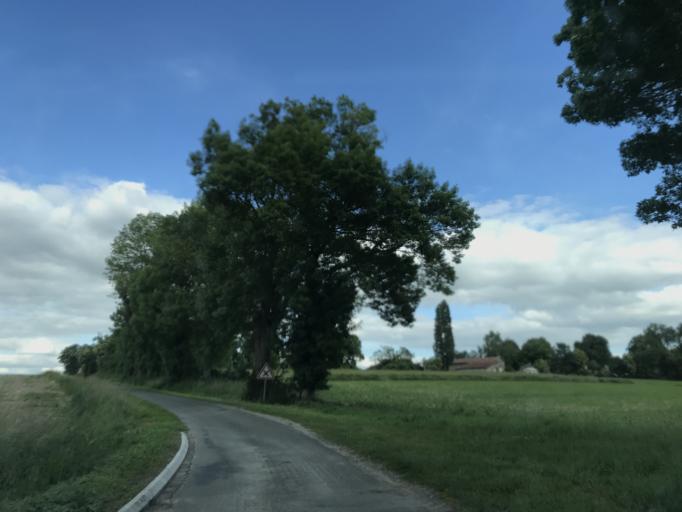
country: FR
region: Aquitaine
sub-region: Departement de la Dordogne
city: Saint-Aulaye
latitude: 45.2608
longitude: 0.1289
